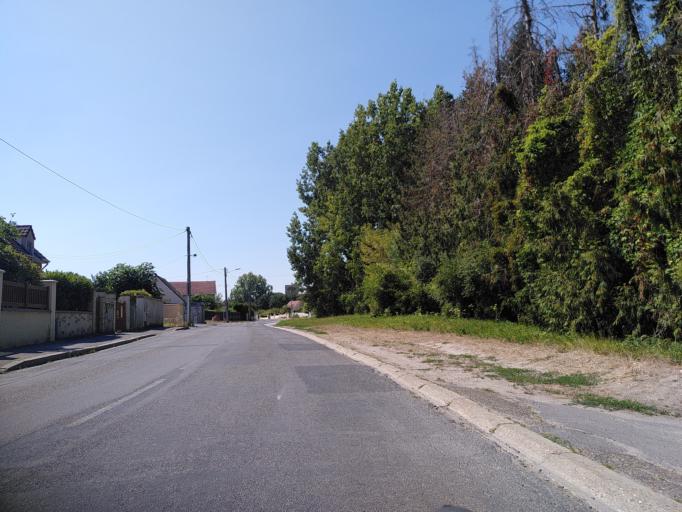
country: FR
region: Ile-de-France
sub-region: Departement de l'Essonne
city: Saint-Germain-les-Arpajon
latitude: 48.6009
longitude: 2.2662
